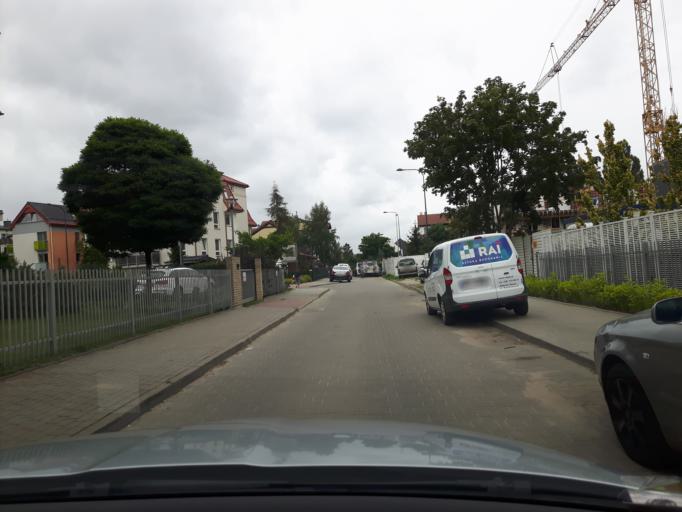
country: PL
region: Pomeranian Voivodeship
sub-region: Sopot
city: Sopot
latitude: 54.4305
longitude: 18.5773
